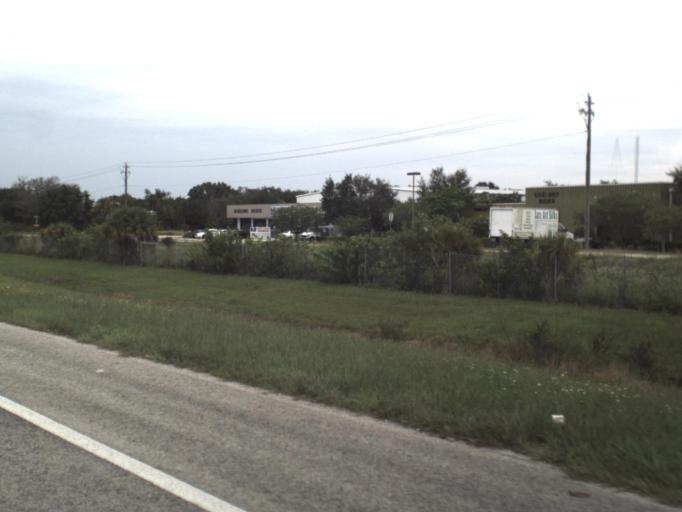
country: US
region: Florida
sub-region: Sarasota County
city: North Sarasota
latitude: 27.3935
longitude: -82.5328
